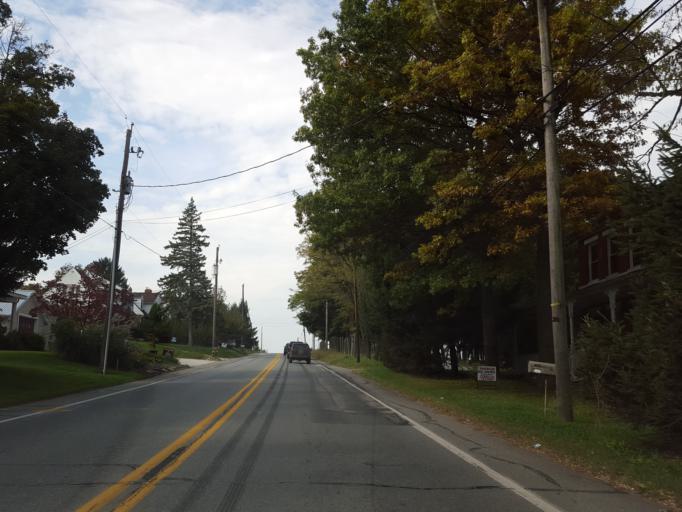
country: US
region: Pennsylvania
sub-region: York County
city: Dallastown
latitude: 39.9068
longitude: -76.6578
